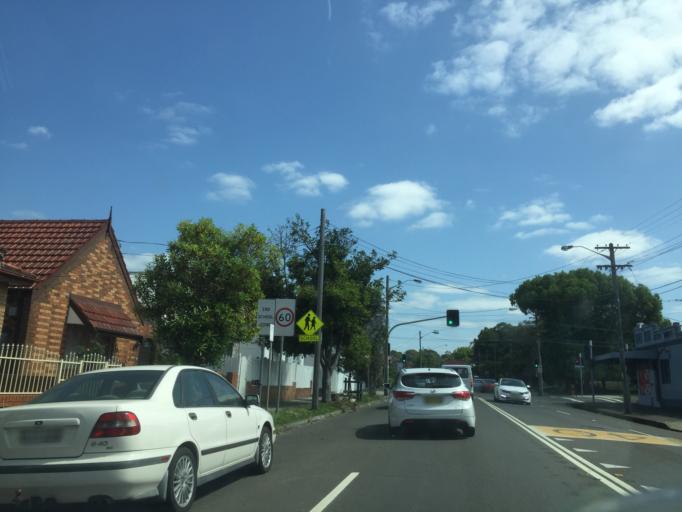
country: AU
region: New South Wales
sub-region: Marrickville
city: Marrickville
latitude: -33.9038
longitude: 151.1555
